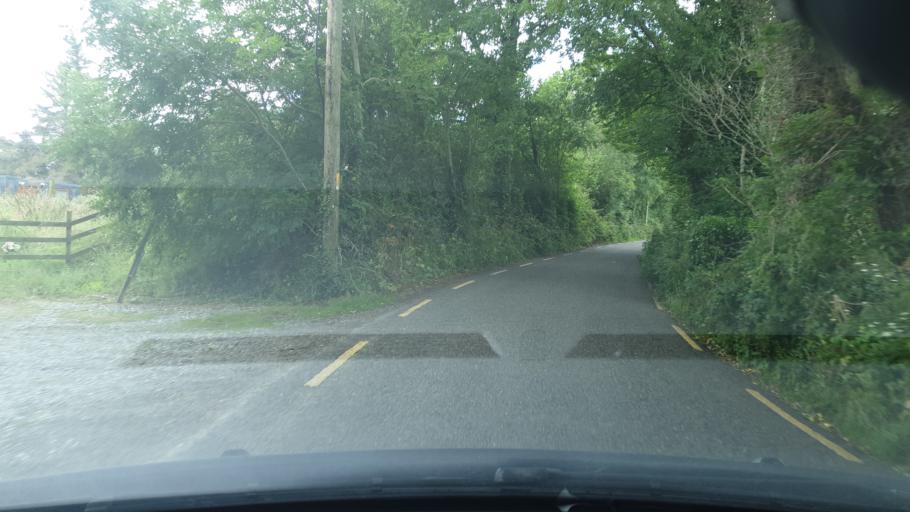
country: IE
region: Munster
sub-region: Ciarrai
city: Tralee
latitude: 52.2473
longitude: -9.6445
